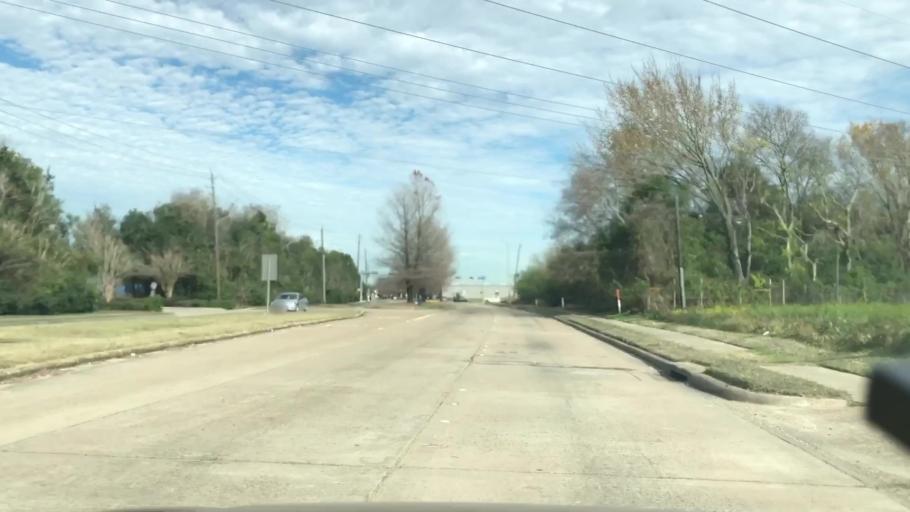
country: US
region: Texas
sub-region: Fort Bend County
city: Missouri City
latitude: 29.6231
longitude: -95.5076
